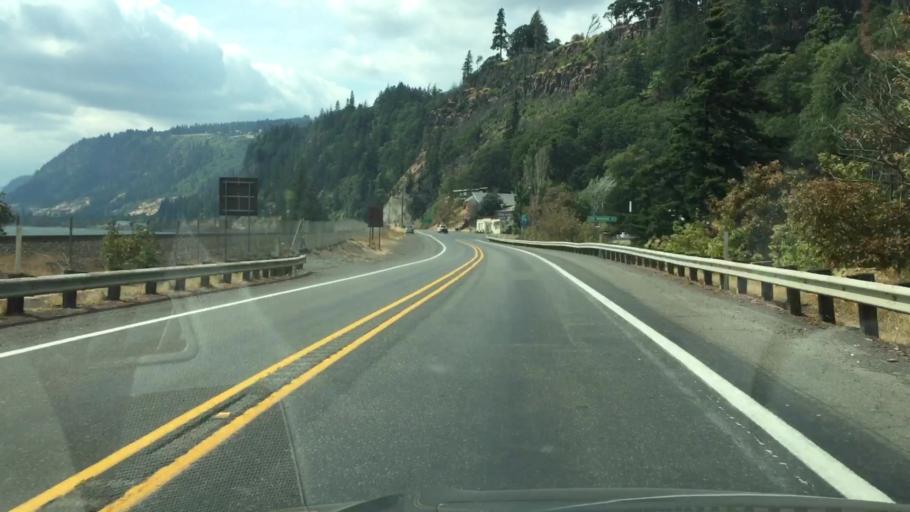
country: US
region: Oregon
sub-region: Hood River County
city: Hood River
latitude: 45.7289
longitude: -121.5227
